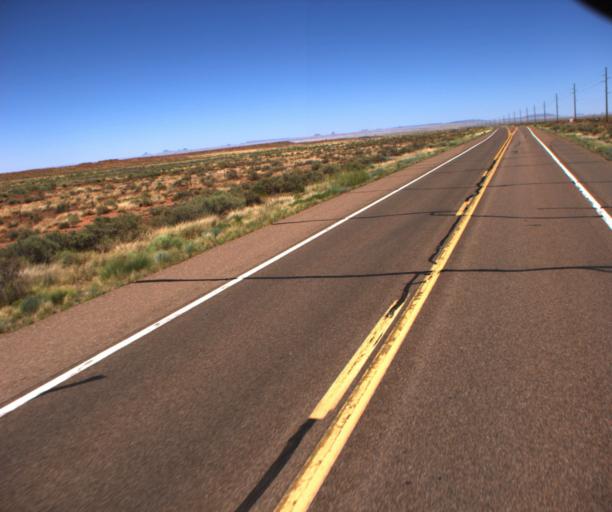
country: US
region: Arizona
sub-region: Coconino County
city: LeChee
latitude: 34.9608
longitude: -110.7438
